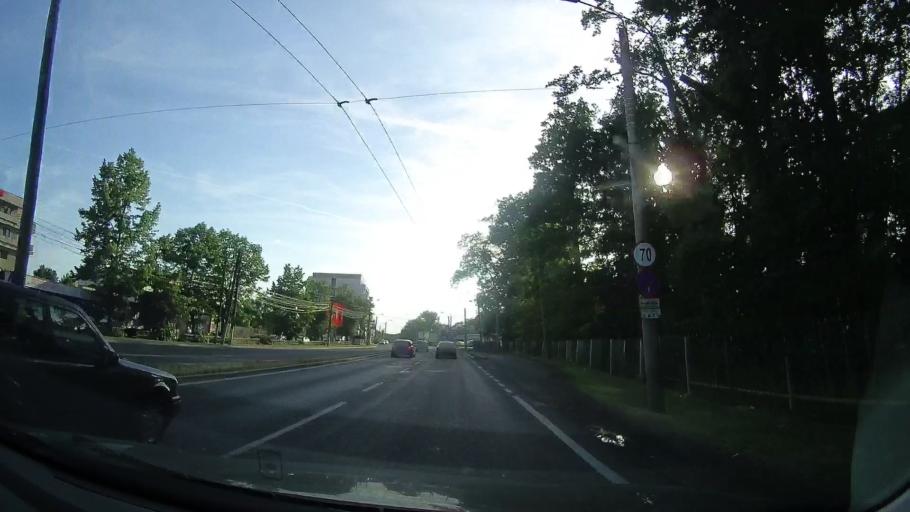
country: RO
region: Timis
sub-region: Comuna Ghiroda
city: Ghiroda
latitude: 45.7696
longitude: 21.2680
